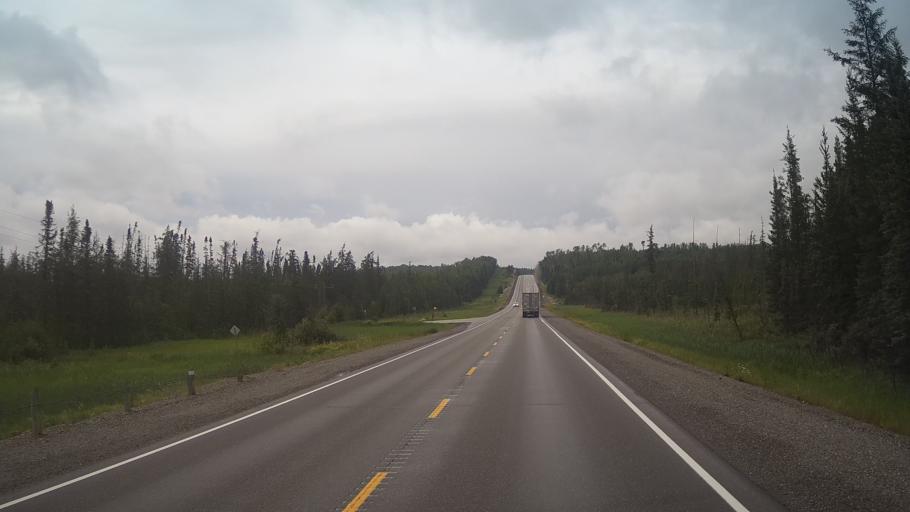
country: CA
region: Ontario
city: Neebing
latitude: 48.6823
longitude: -89.8926
